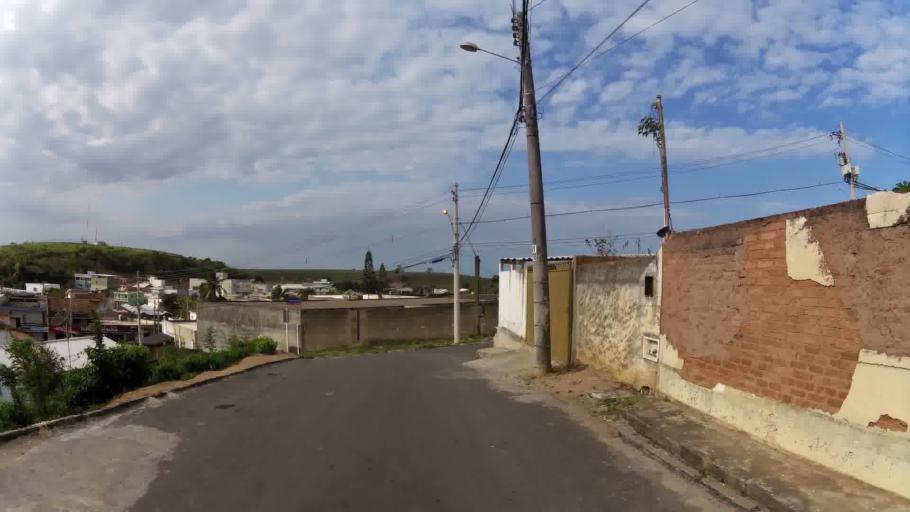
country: BR
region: Espirito Santo
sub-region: Itapemirim
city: Itapemirim
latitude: -21.0107
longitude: -40.8318
